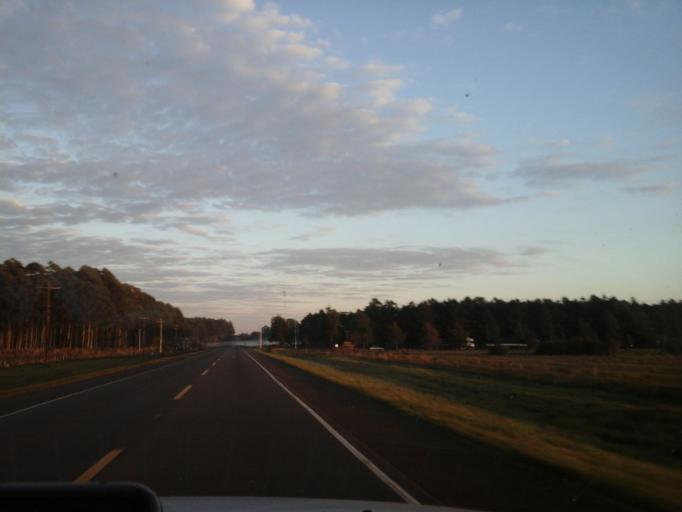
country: PY
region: Itapua
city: General Delgado
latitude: -27.0627
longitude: -56.6236
